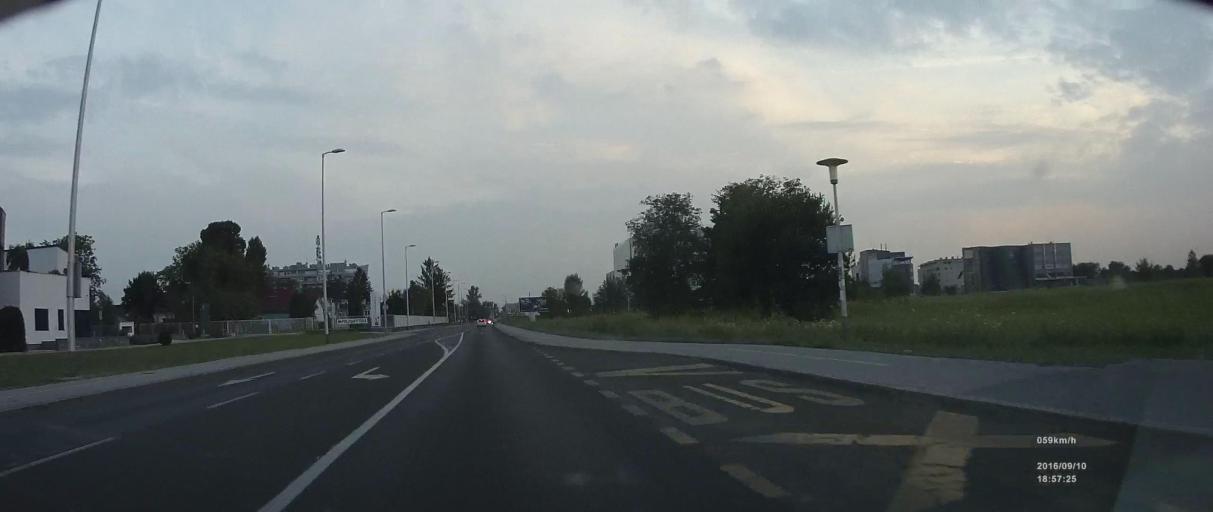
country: HR
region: Grad Zagreb
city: Novi Zagreb
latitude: 45.7668
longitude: 15.9807
